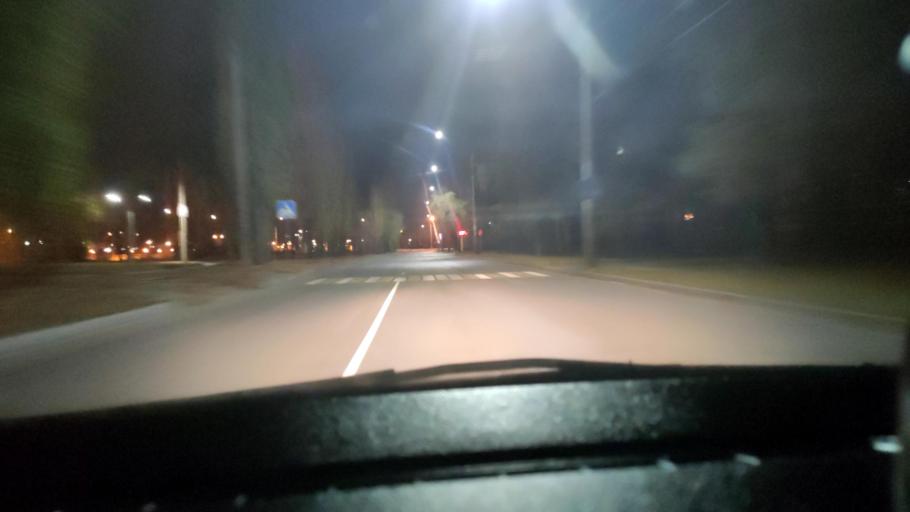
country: RU
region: Voronezj
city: Voronezh
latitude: 51.6479
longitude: 39.1355
